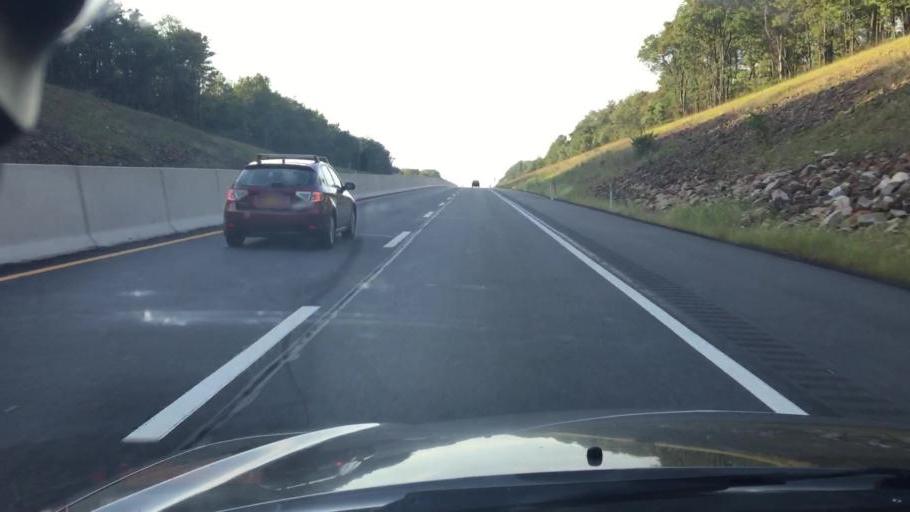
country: US
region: Pennsylvania
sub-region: Carbon County
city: Towamensing Trails
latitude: 41.0316
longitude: -75.6549
